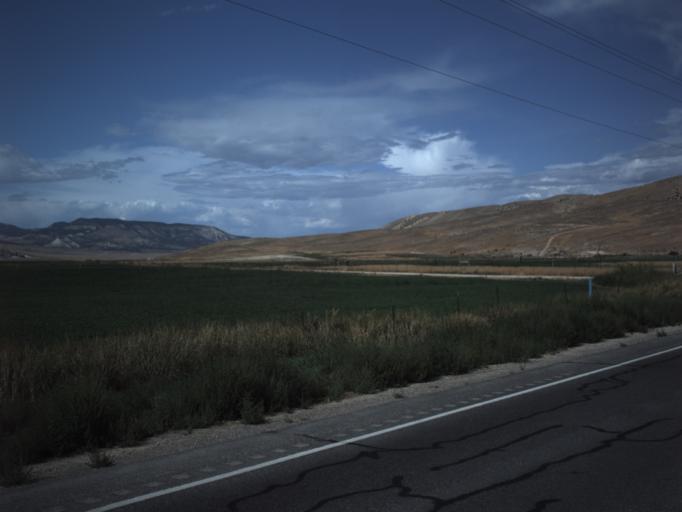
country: US
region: Utah
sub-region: Sanpete County
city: Gunnison
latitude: 39.1579
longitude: -111.7583
